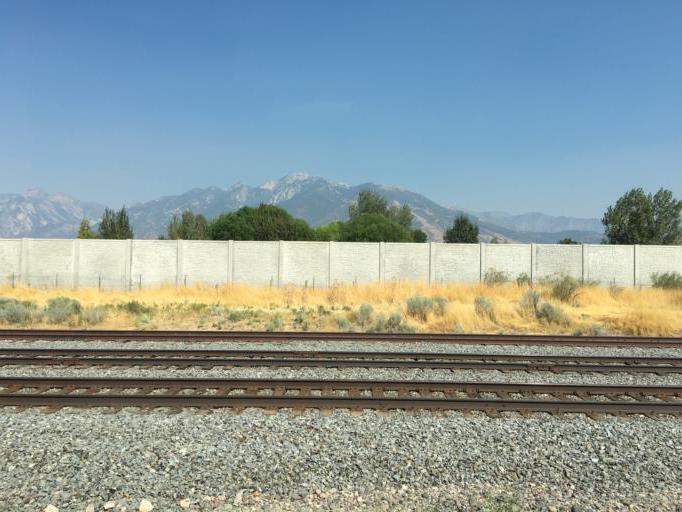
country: US
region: Utah
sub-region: Salt Lake County
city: Riverton
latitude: 40.5153
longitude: -111.9043
